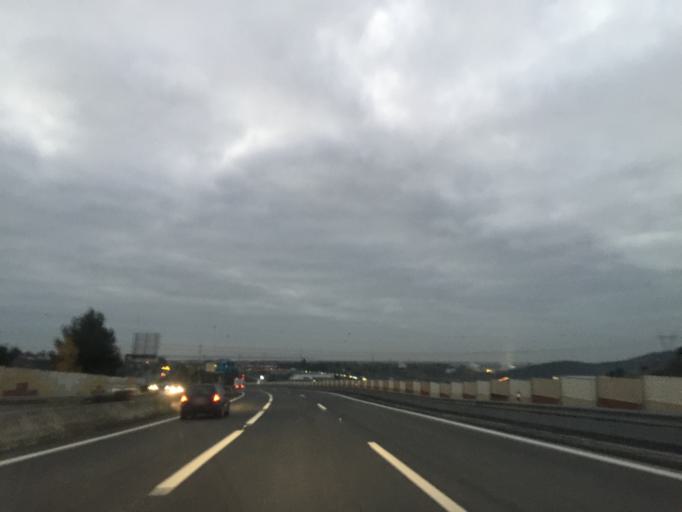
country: PT
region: Lisbon
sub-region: Vila Franca de Xira
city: Vialonga
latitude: 38.8982
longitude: -9.0550
